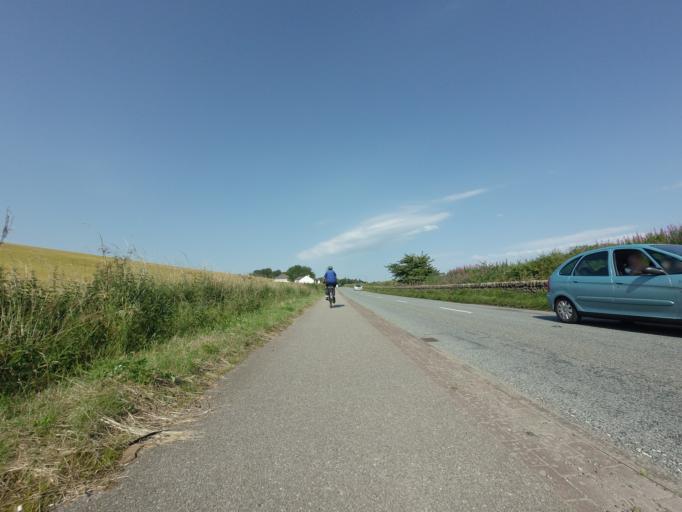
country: GB
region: Scotland
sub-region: Highland
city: Alness
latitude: 57.6875
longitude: -4.2822
